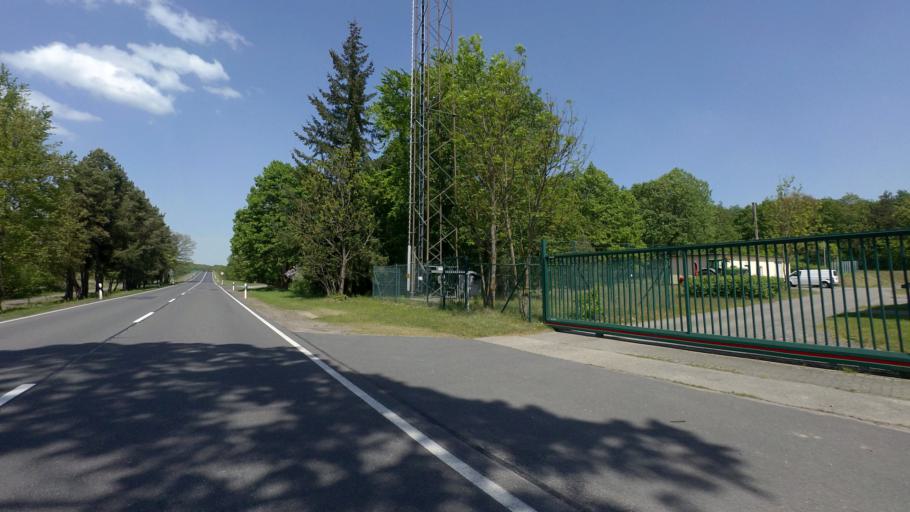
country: DE
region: Mecklenburg-Vorpommern
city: Neustrelitz
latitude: 53.4064
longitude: 13.0425
